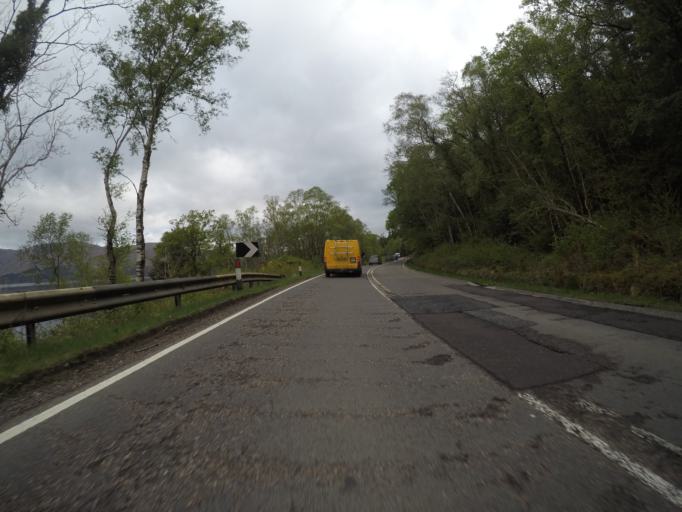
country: GB
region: Scotland
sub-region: Highland
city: Fort William
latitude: 56.7432
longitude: -5.2053
